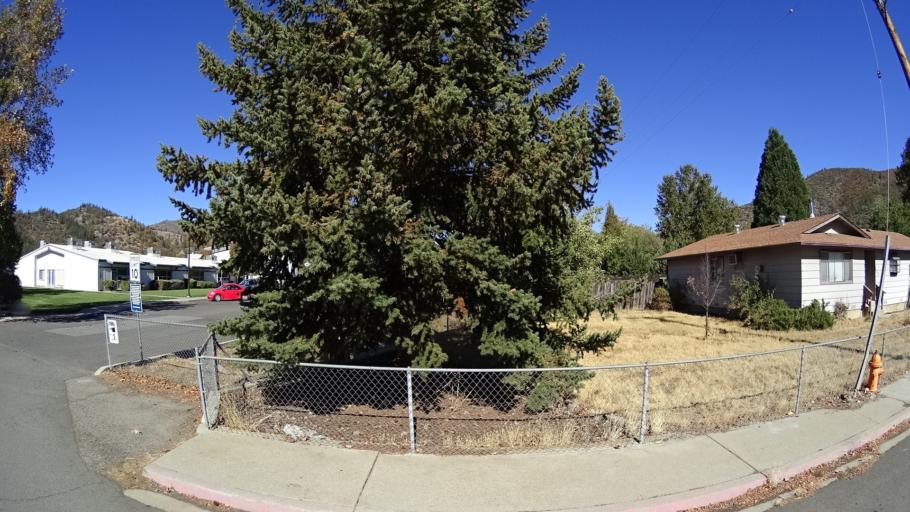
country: US
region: California
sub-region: Siskiyou County
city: Yreka
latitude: 41.6094
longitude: -122.8432
